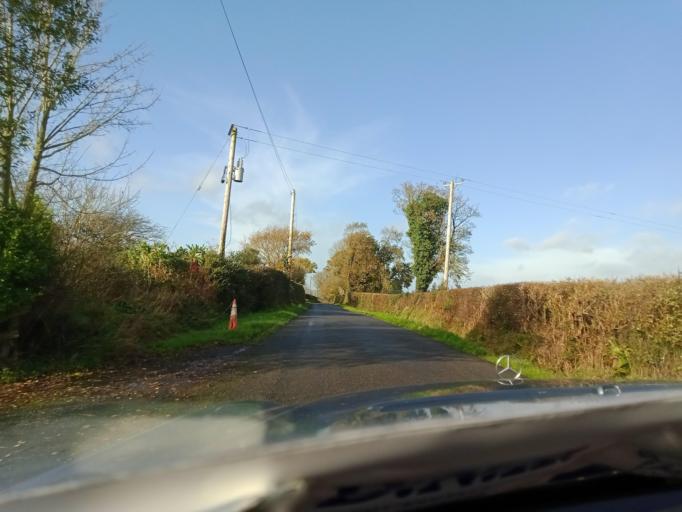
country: IE
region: Leinster
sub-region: Kilkenny
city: Mooncoin
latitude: 52.3309
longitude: -7.2559
